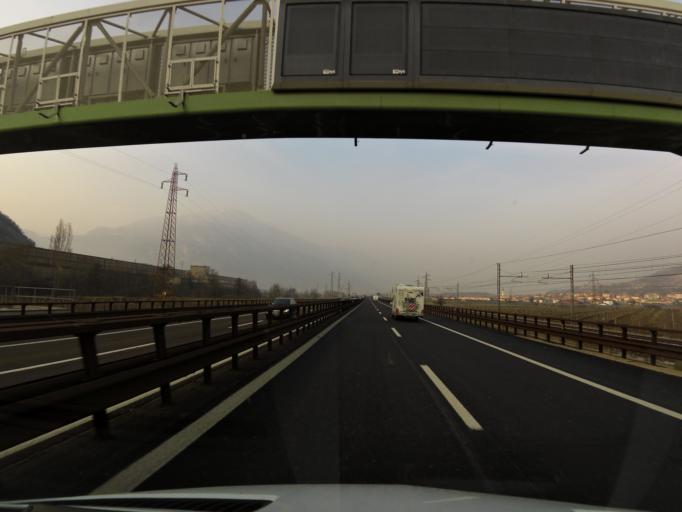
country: IT
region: Trentino-Alto Adige
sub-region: Provincia di Trento
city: Marco
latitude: 45.8332
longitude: 11.0031
